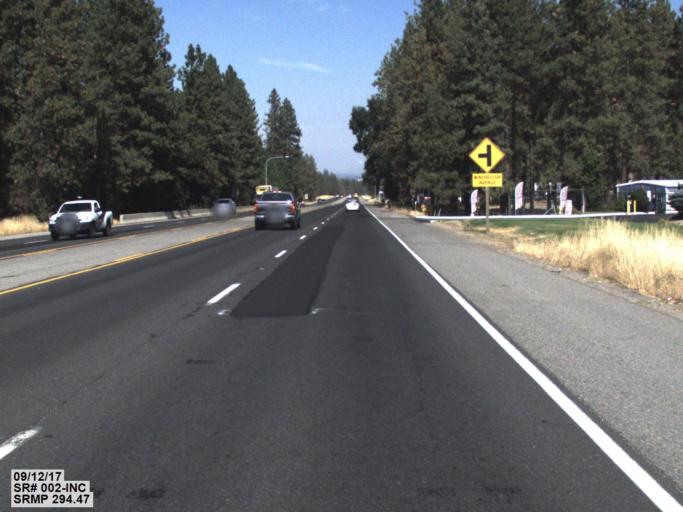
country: US
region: Washington
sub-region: Spokane County
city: Country Homes
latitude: 47.7591
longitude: -117.3928
